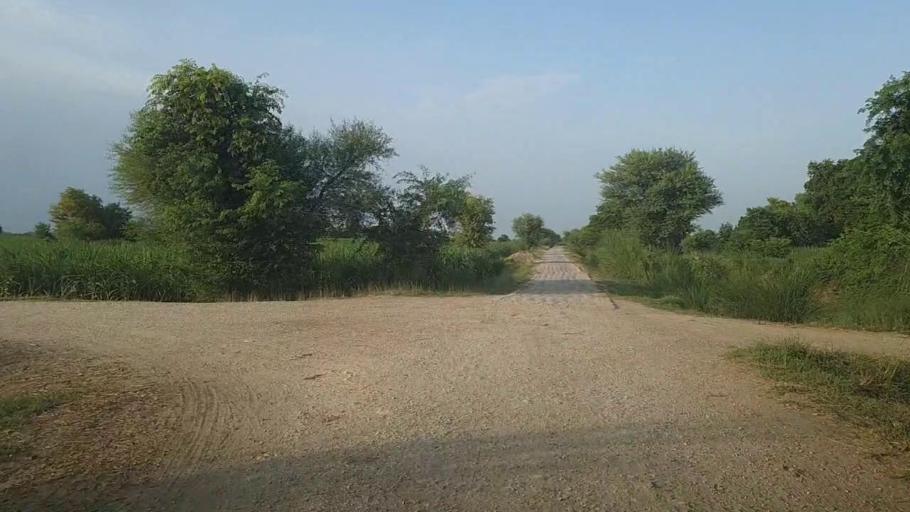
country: PK
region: Sindh
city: Ubauro
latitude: 28.3695
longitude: 69.7987
